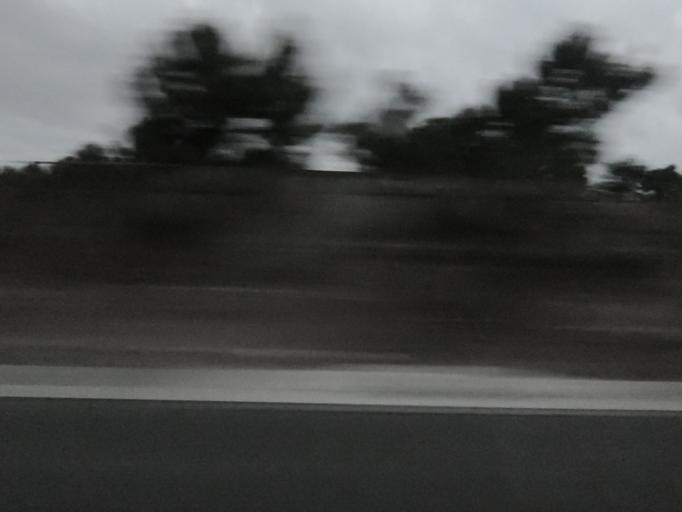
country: PT
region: Setubal
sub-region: Seixal
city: Aldeia de Paio Pires
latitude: 38.5894
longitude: -9.0879
